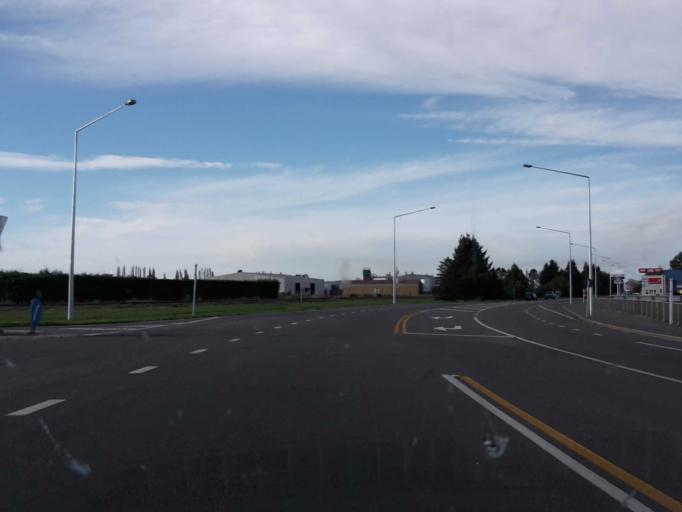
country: NZ
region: Canterbury
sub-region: Ashburton District
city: Tinwald
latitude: -44.0019
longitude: 171.5702
